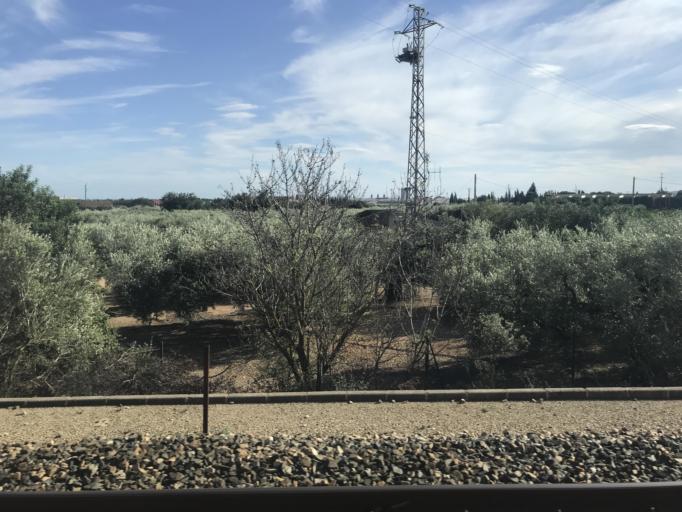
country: ES
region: Catalonia
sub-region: Provincia de Tarragona
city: Camarles
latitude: 40.7590
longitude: 0.6307
